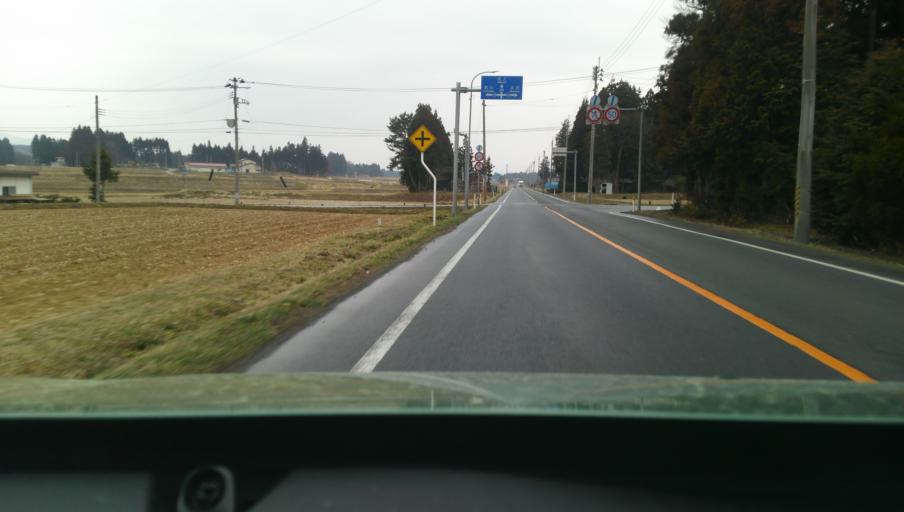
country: JP
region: Iwate
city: Mizusawa
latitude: 39.0690
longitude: 141.0630
